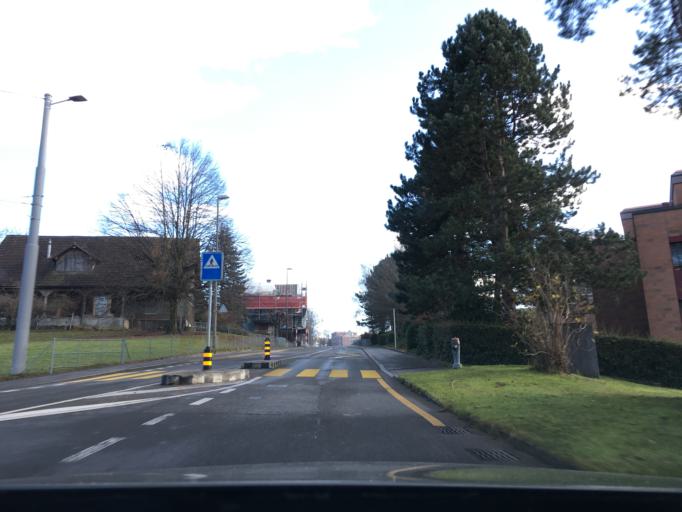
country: CH
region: Lucerne
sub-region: Lucerne-Land District
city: Adligenswil
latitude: 47.0522
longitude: 8.3499
